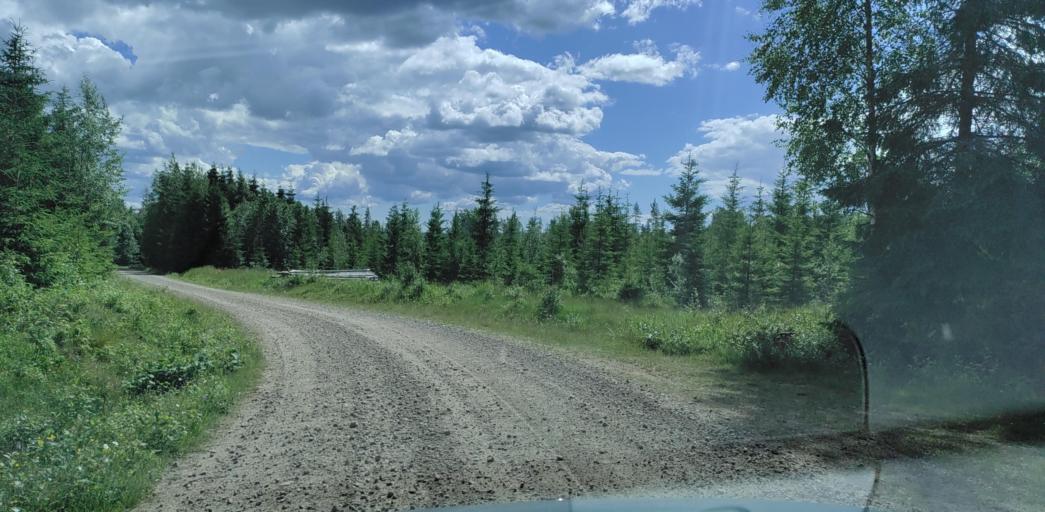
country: SE
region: Vaermland
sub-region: Hagfors Kommun
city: Ekshaerad
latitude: 60.0477
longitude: 13.3090
